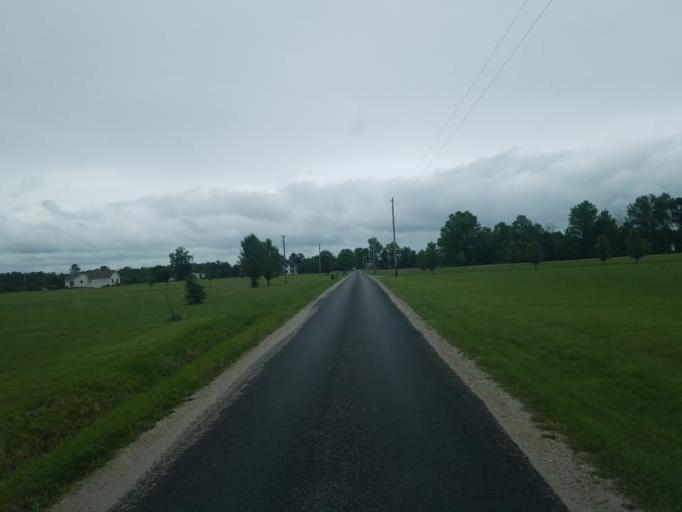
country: US
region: Ohio
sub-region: Marion County
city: Marion
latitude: 40.5376
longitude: -83.0144
